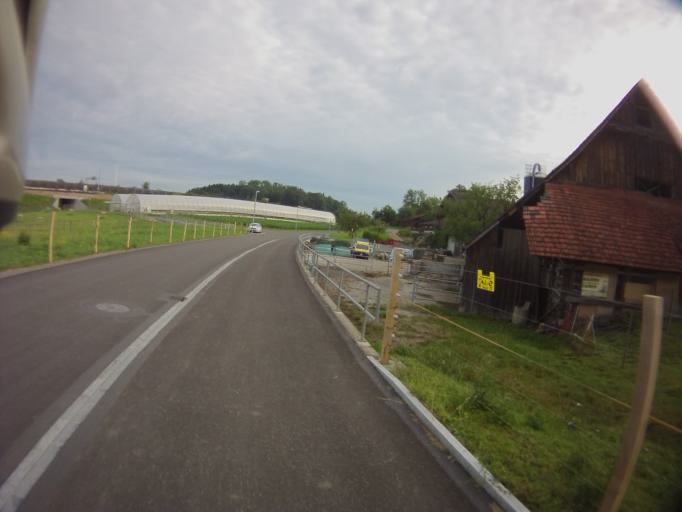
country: CH
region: Zug
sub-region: Zug
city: Steinhausen
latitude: 47.2051
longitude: 8.4703
